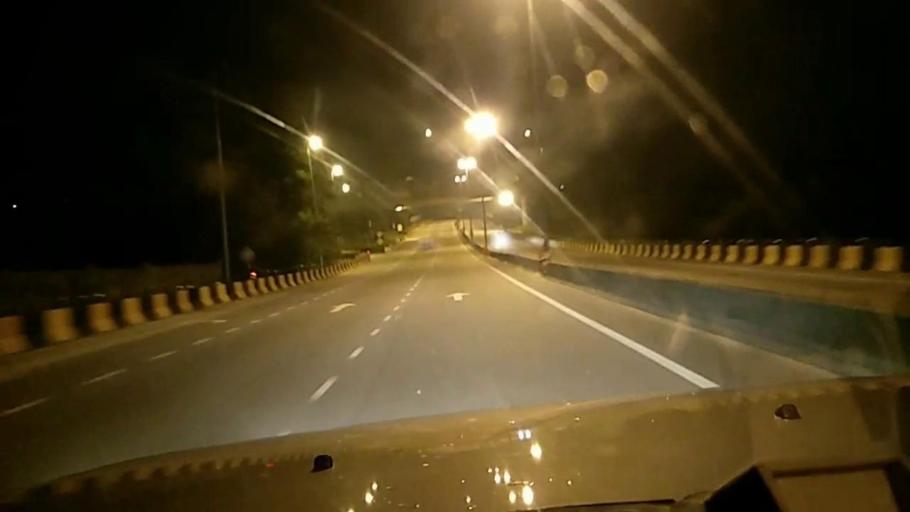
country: MY
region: Selangor
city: Kampung Baru Subang
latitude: 3.1340
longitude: 101.4994
